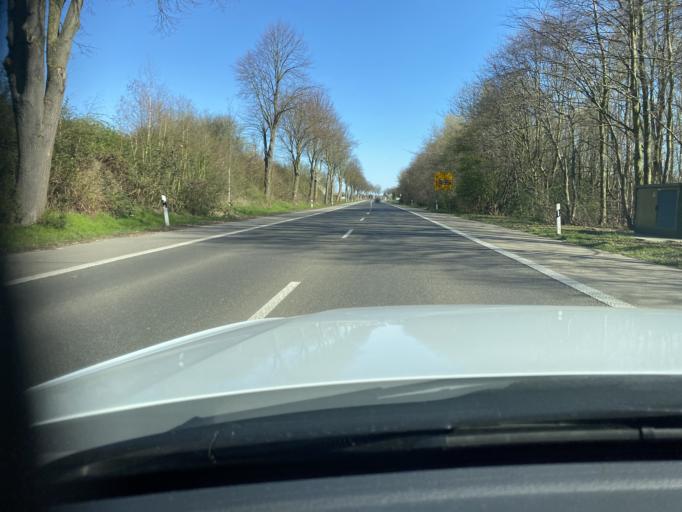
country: DE
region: North Rhine-Westphalia
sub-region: Regierungsbezirk Dusseldorf
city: Neubrueck
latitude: 51.1474
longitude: 6.6562
